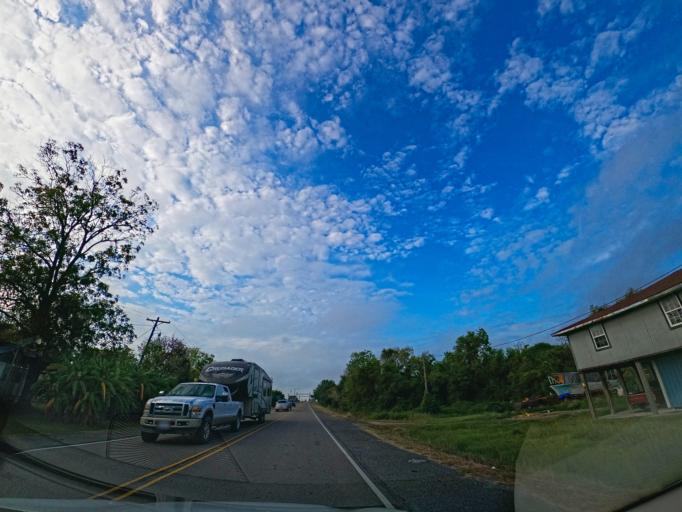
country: US
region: Louisiana
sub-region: Terrebonne Parish
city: Chauvin
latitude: 29.3881
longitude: -90.6191
